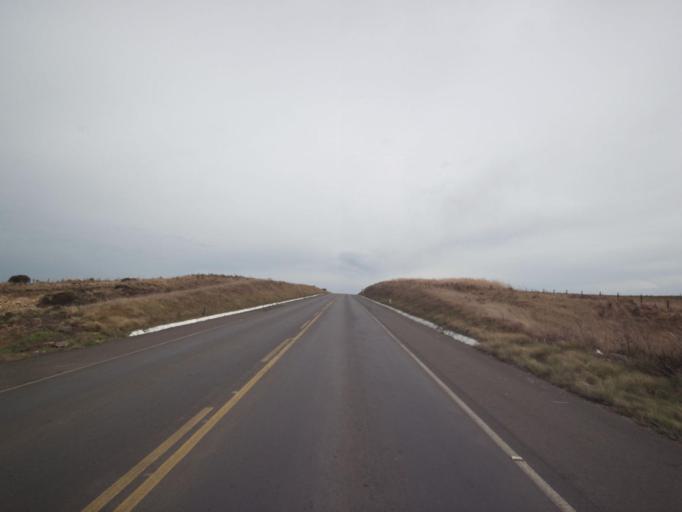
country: BR
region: Parana
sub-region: Palmas
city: Palmas
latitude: -26.7154
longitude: -51.6152
